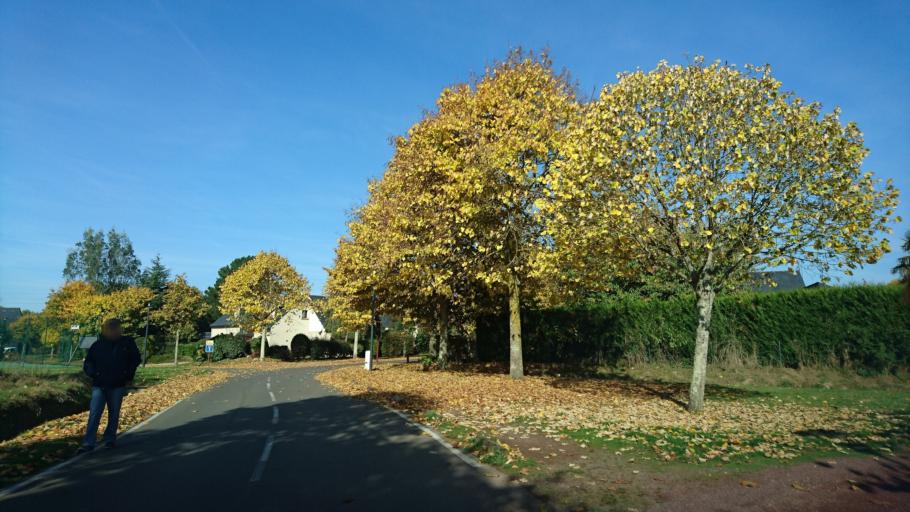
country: FR
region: Brittany
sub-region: Departement d'Ille-et-Vilaine
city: Bruz
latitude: 48.0392
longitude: -1.7650
